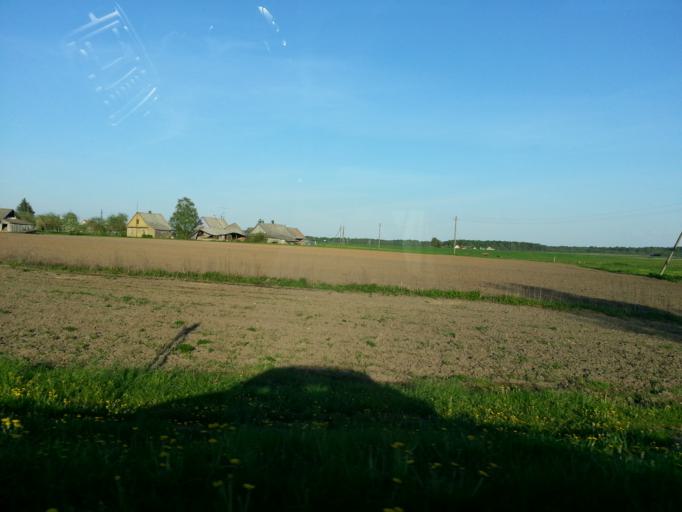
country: LT
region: Vilnius County
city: Ukmerge
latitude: 55.4265
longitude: 24.5893
